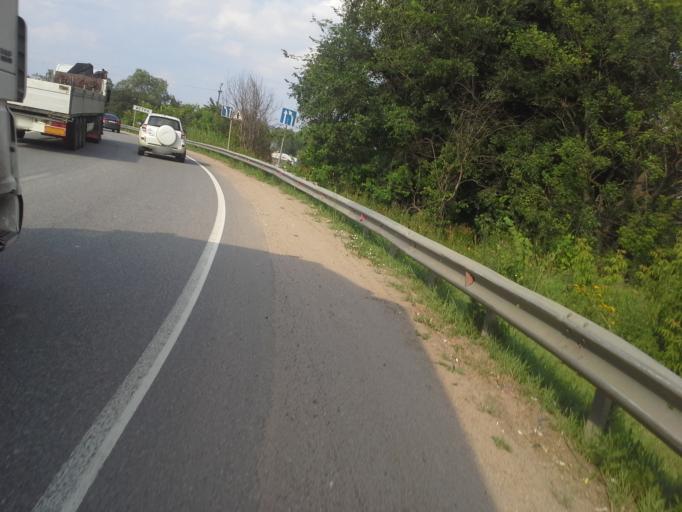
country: RU
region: Moskovskaya
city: Istra
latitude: 55.9074
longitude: 36.8102
